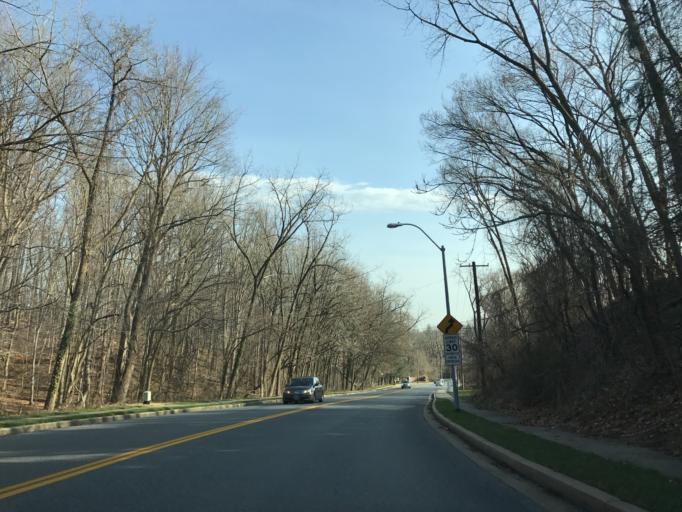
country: US
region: Maryland
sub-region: Baltimore County
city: Lutherville
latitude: 39.3752
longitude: -76.6605
